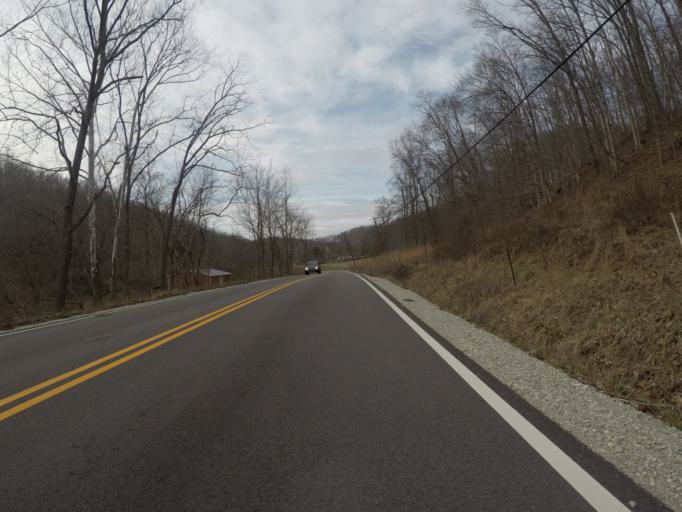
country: US
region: Ohio
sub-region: Lawrence County
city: Burlington
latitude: 38.4521
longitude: -82.5187
